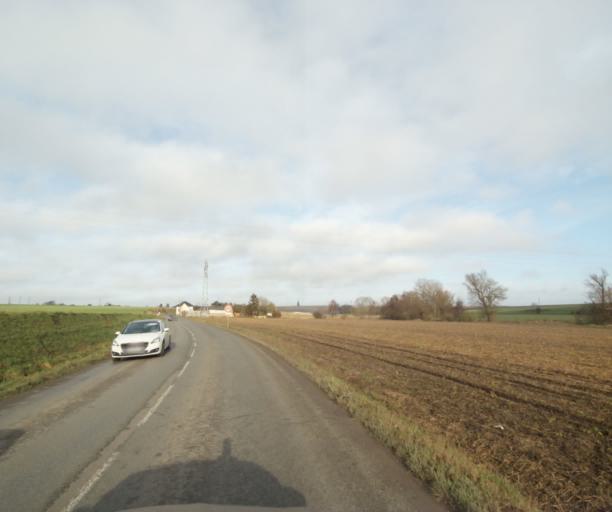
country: FR
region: Nord-Pas-de-Calais
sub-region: Departement du Nord
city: Thiant
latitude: 50.2922
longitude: 3.4484
